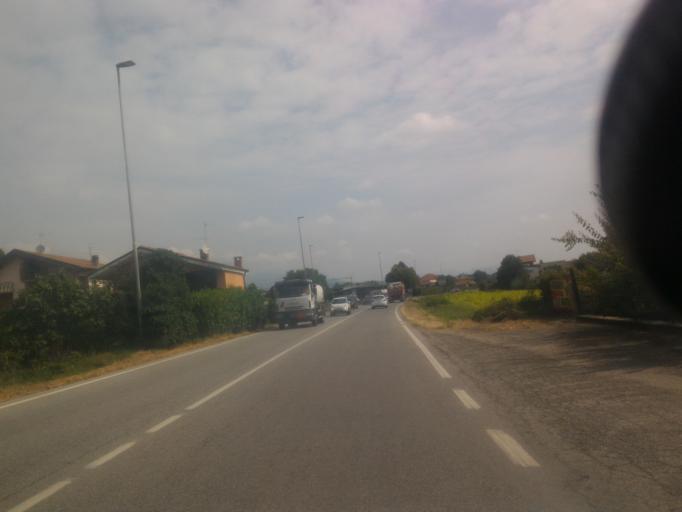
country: IT
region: Piedmont
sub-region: Provincia di Torino
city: Bricherasio
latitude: 44.8376
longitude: 7.3052
